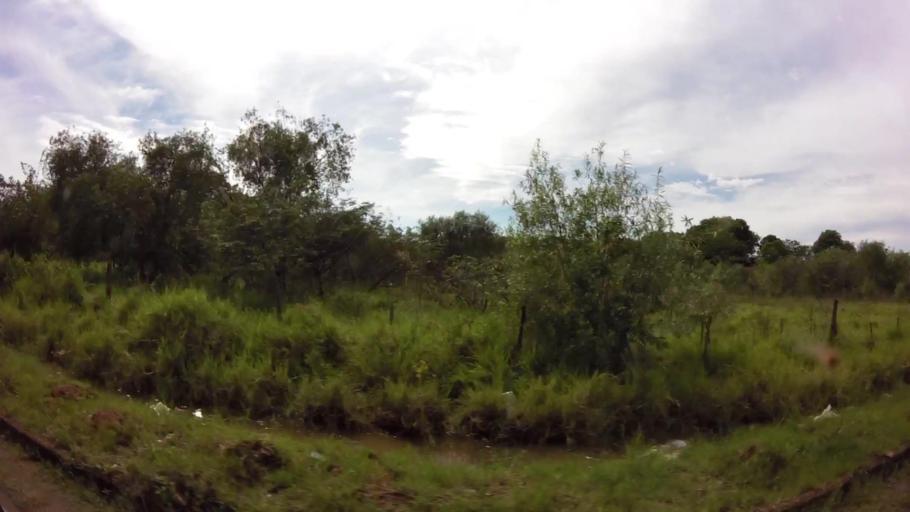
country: PY
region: Central
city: Limpio
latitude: -25.1785
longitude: -57.4739
